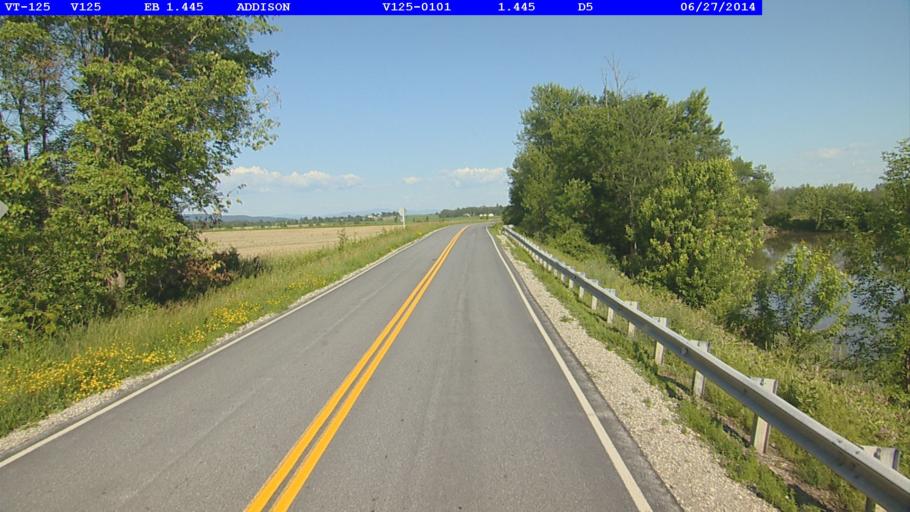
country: US
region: New York
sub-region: Essex County
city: Port Henry
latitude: 44.0254
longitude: -73.3966
